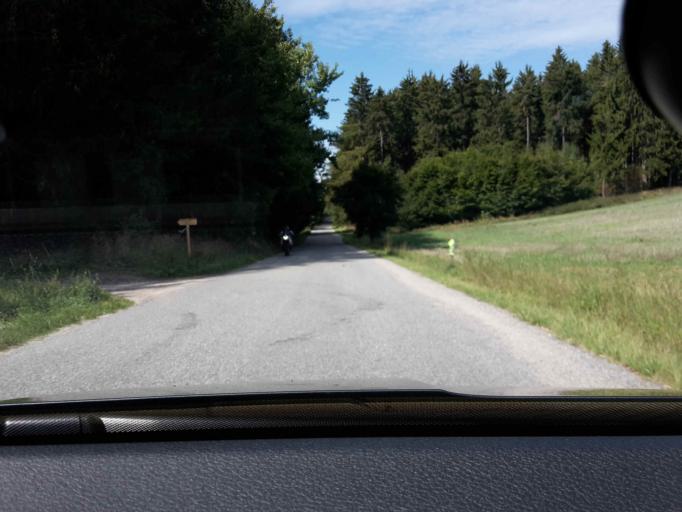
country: CZ
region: Vysocina
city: Zeletava
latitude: 49.1281
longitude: 15.6018
